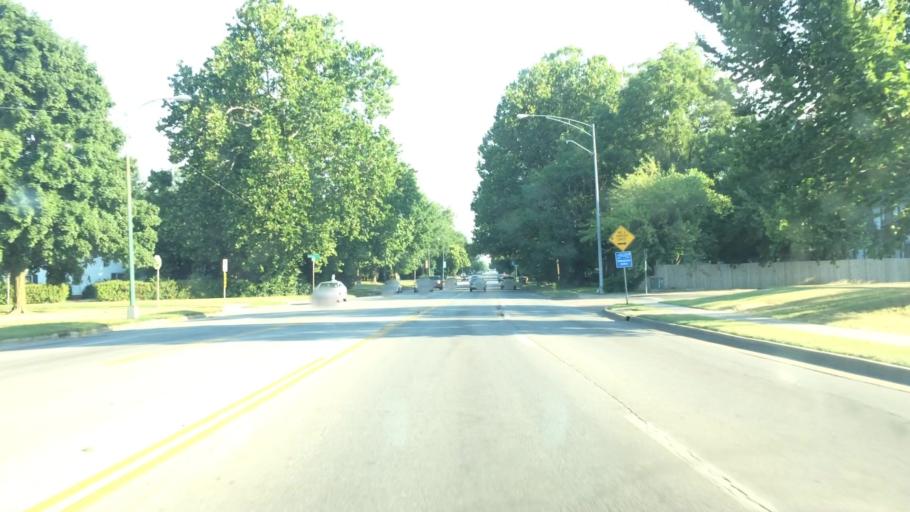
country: US
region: Missouri
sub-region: Greene County
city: Springfield
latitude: 37.1957
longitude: -93.2763
